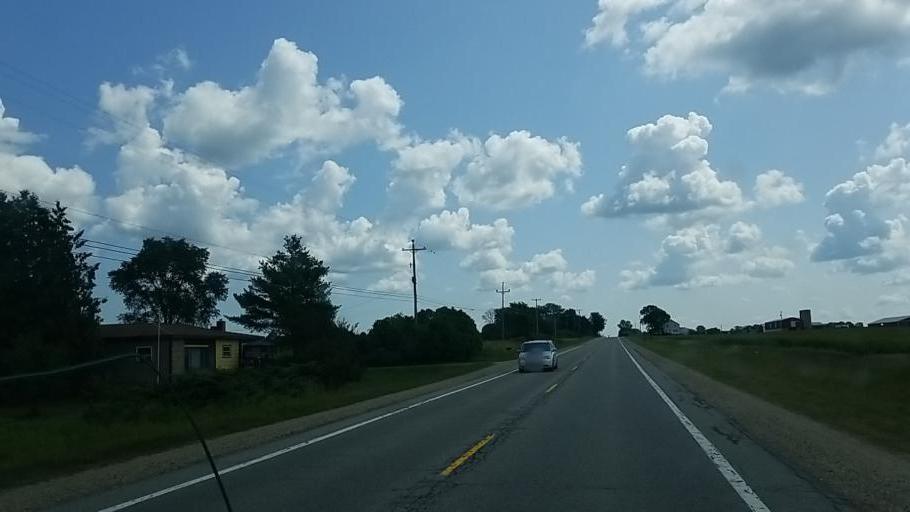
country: US
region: Michigan
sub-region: Muskegon County
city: Ravenna
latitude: 43.2352
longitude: -85.9393
